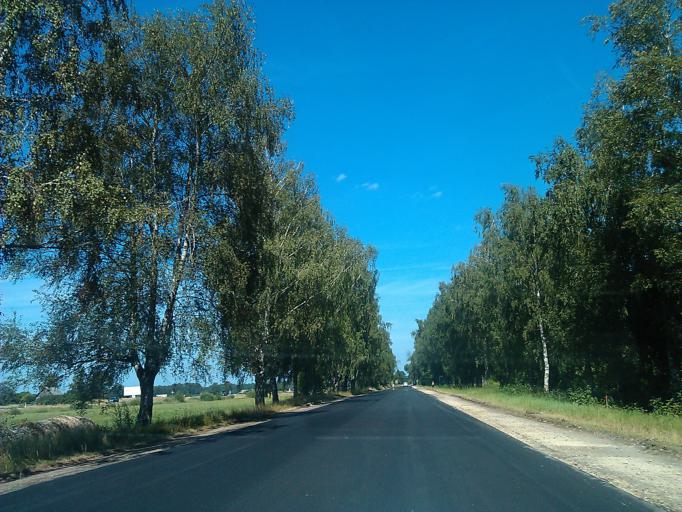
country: LV
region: Adazi
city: Adazi
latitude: 57.0913
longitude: 24.3143
